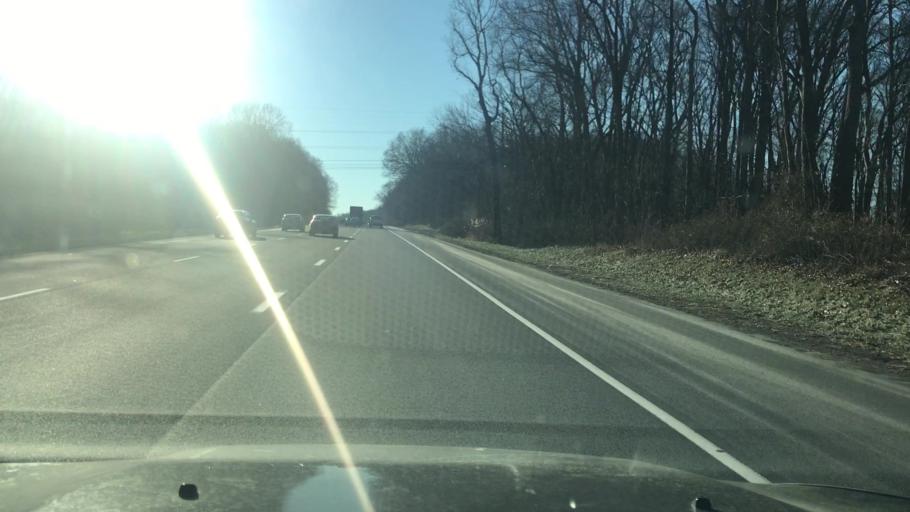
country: US
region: Connecticut
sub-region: Hartford County
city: Plainville
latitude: 41.6252
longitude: -72.8845
